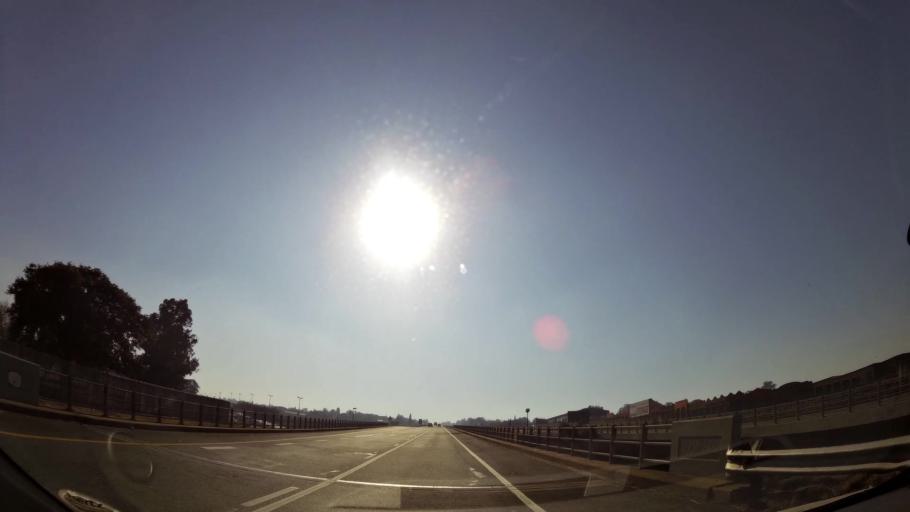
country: ZA
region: Mpumalanga
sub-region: Nkangala District Municipality
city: Witbank
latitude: -25.9172
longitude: 29.2339
